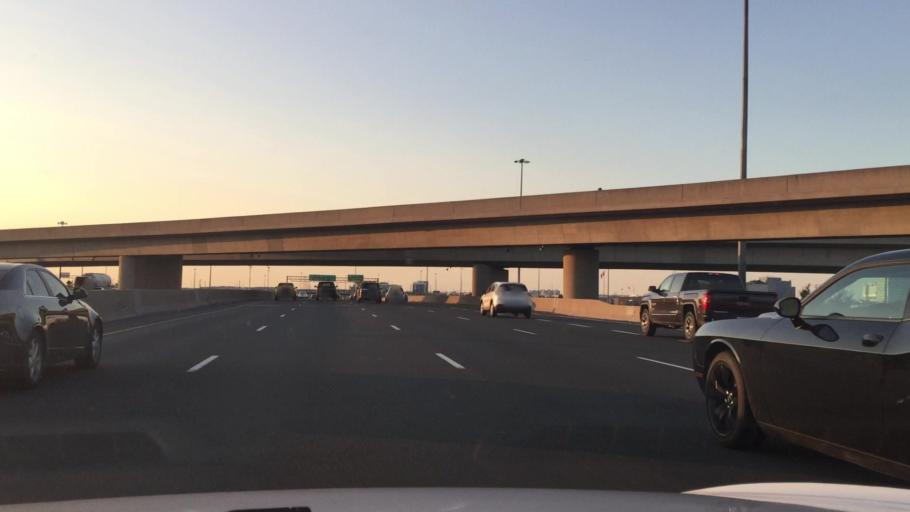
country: CA
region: Ontario
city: Concord
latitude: 43.7819
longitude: -79.5369
